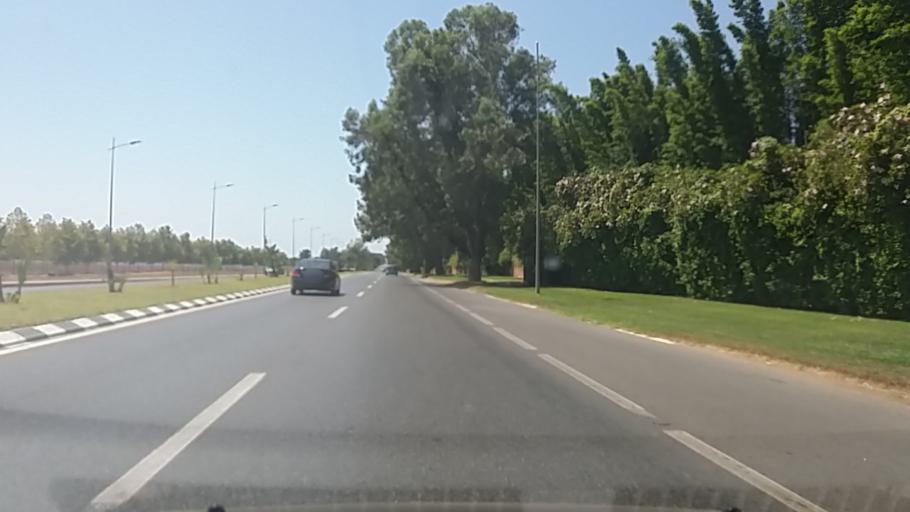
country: MA
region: Rabat-Sale-Zemmour-Zaer
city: Sale
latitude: 34.0294
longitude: -6.7390
